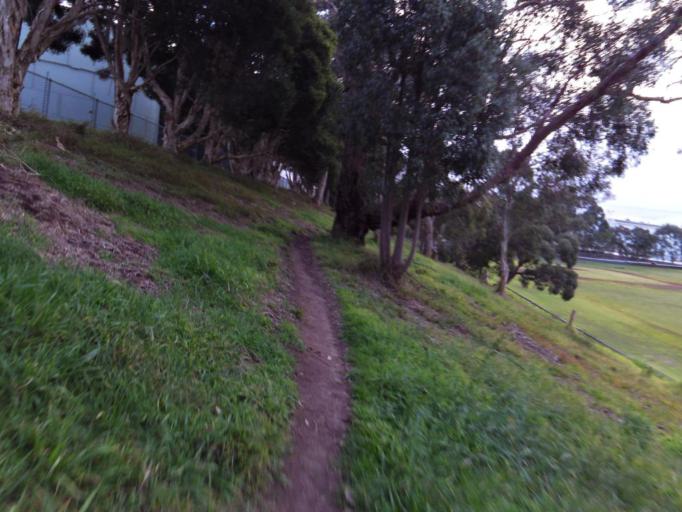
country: AU
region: Victoria
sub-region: Knox
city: Wantirna
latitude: -37.8295
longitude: 145.2218
